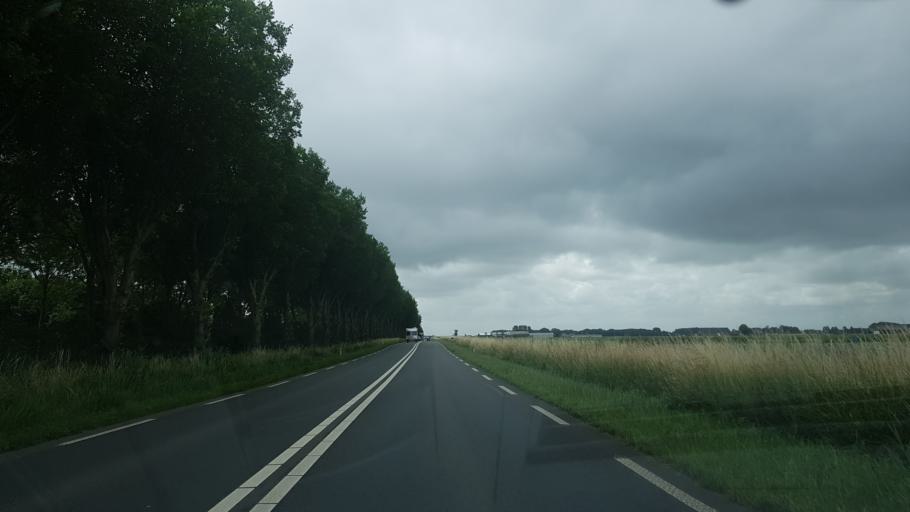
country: NL
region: North Holland
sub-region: Gemeente Medemblik
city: Medemblik
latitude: 52.7447
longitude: 5.1087
